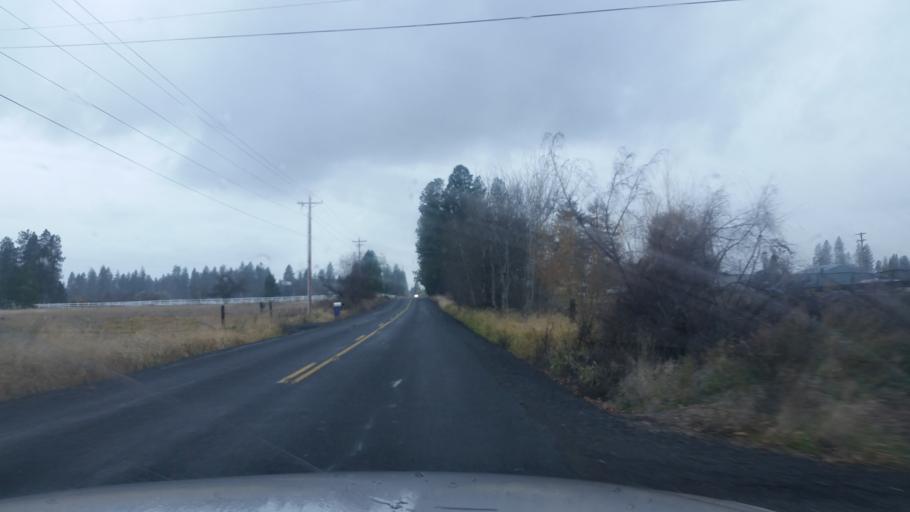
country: US
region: Washington
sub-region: Spokane County
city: Spokane
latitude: 47.5944
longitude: -117.4797
